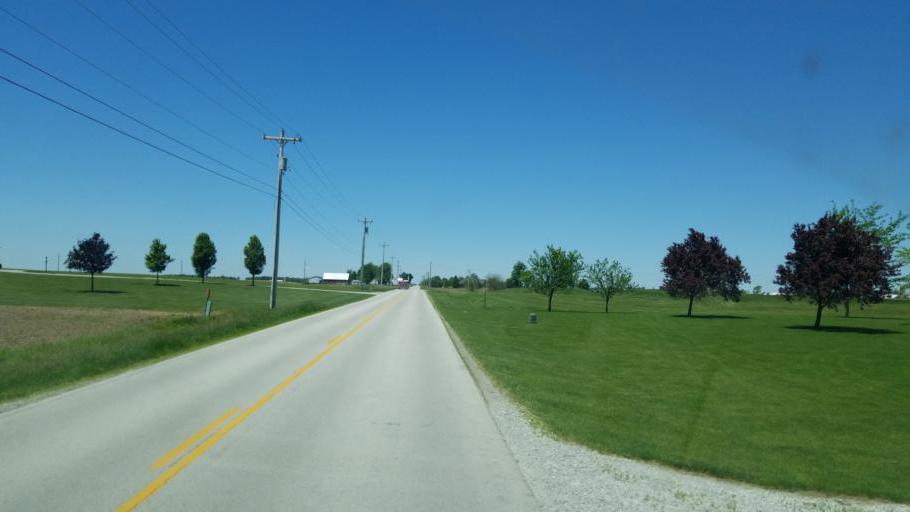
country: US
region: Ohio
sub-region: Auglaize County
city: Minster
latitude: 40.3856
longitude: -84.3991
